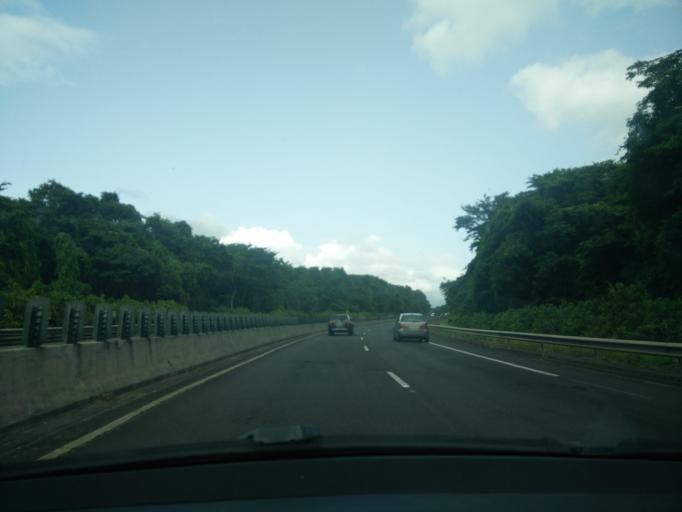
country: GP
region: Guadeloupe
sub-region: Guadeloupe
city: Les Abymes
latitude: 16.2733
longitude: -61.5353
